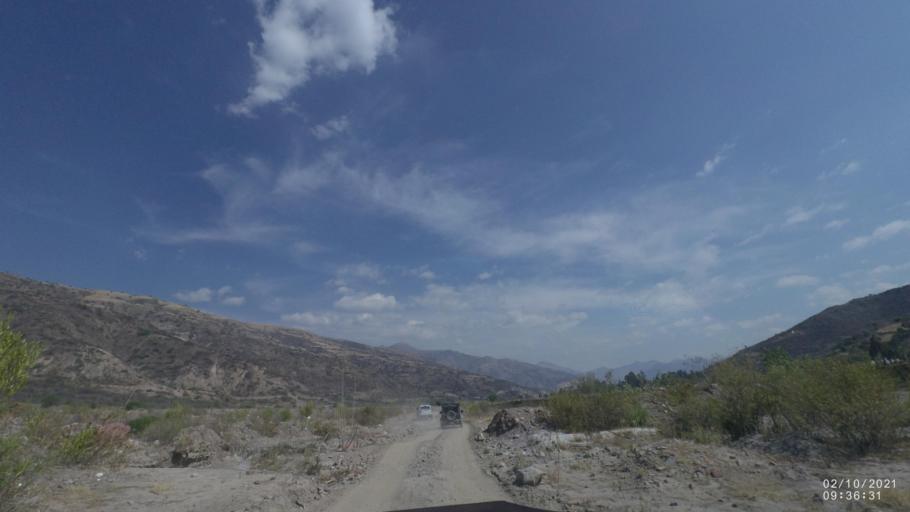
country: BO
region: Cochabamba
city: Irpa Irpa
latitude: -17.8326
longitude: -66.3215
